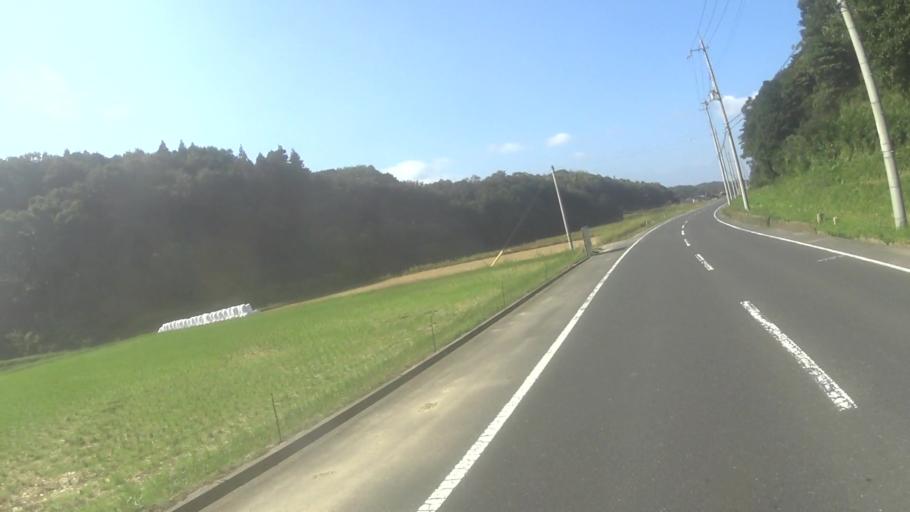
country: JP
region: Kyoto
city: Miyazu
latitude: 35.6712
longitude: 135.0569
